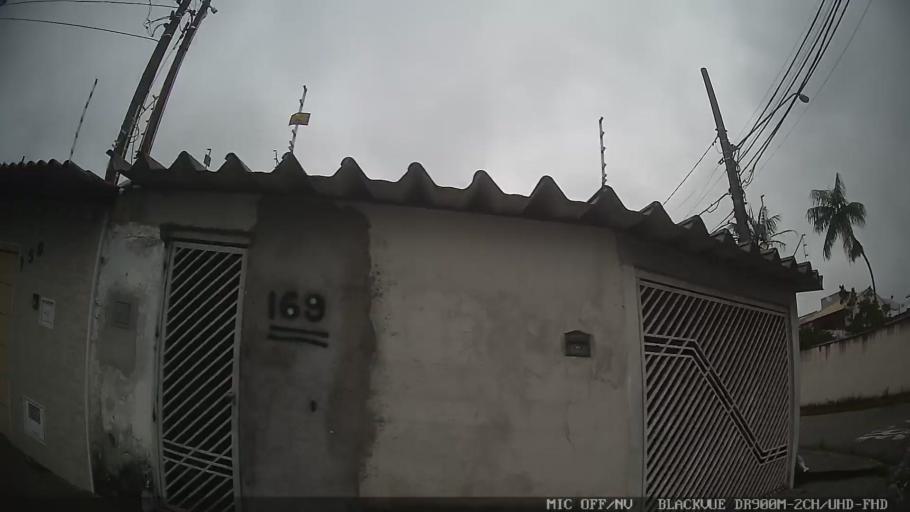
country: BR
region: Sao Paulo
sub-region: Mogi das Cruzes
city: Mogi das Cruzes
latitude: -23.5224
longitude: -46.1652
